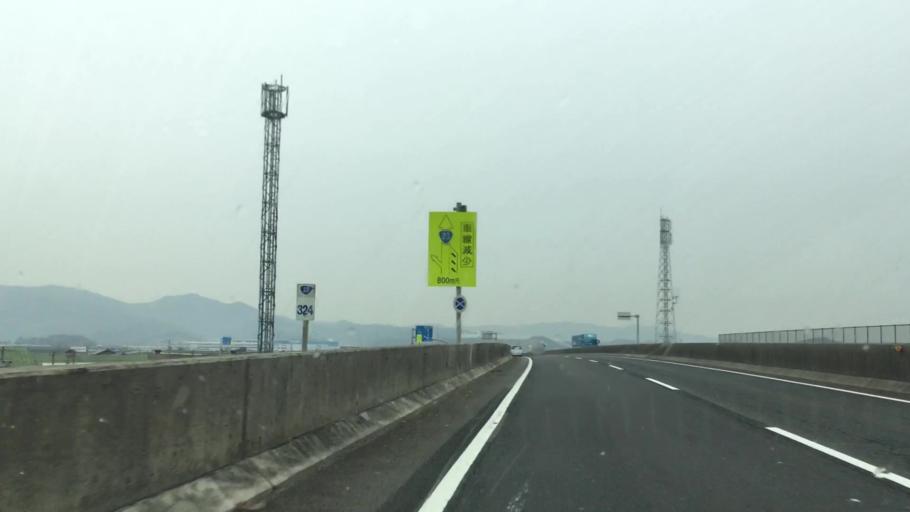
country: JP
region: Aichi
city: Nishio
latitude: 34.8735
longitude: 137.0826
